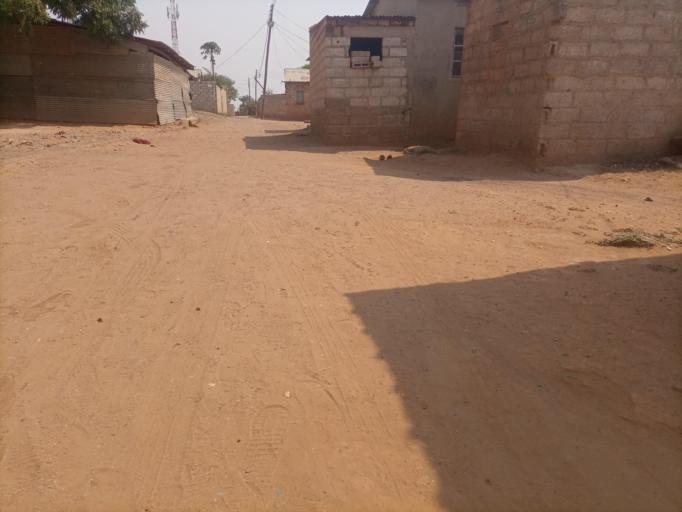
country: ZM
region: Lusaka
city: Lusaka
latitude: -15.4039
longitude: 28.3804
